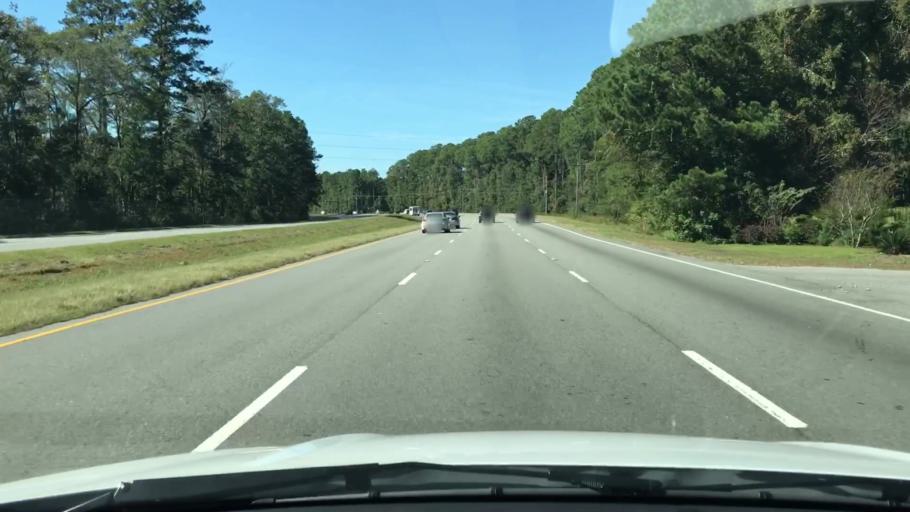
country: US
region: South Carolina
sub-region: Beaufort County
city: Bluffton
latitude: 32.2893
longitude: -80.8965
